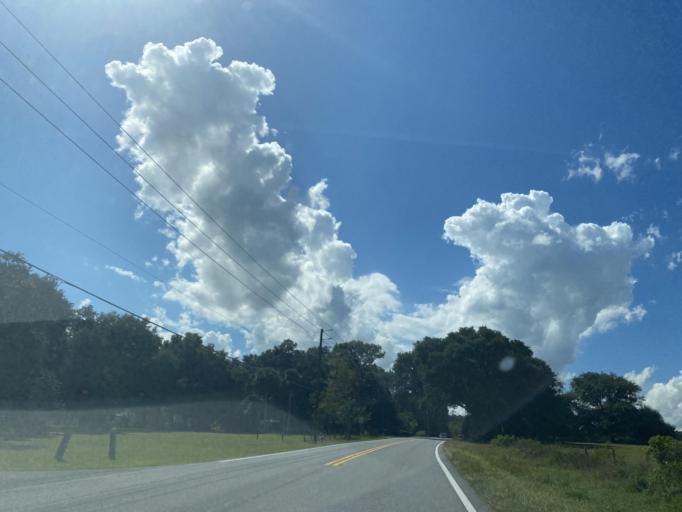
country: US
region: Florida
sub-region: Lake County
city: Lady Lake
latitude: 28.9823
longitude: -81.9084
